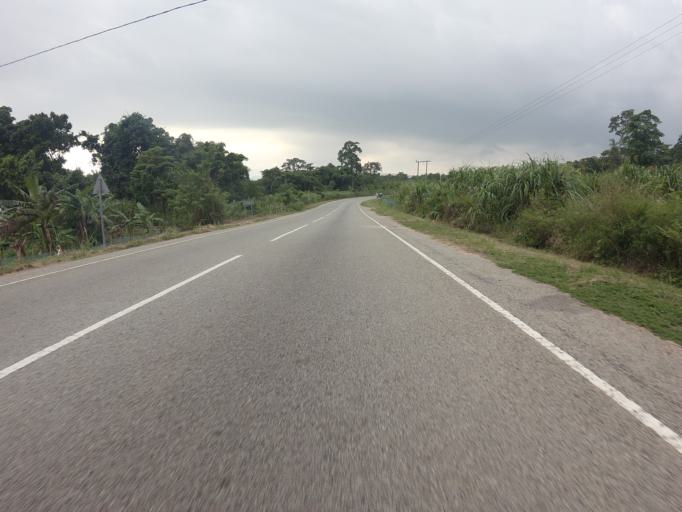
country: GH
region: Volta
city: Ho
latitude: 6.7595
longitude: 0.4798
